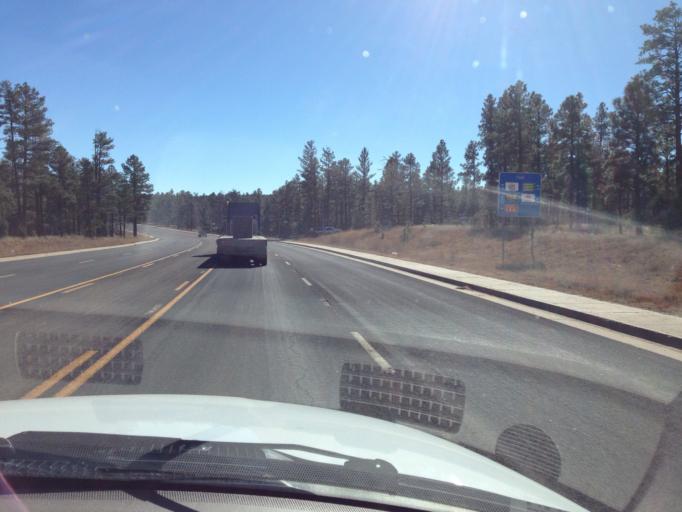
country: US
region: Arizona
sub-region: Navajo County
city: Show Low
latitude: 34.2469
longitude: -110.0711
